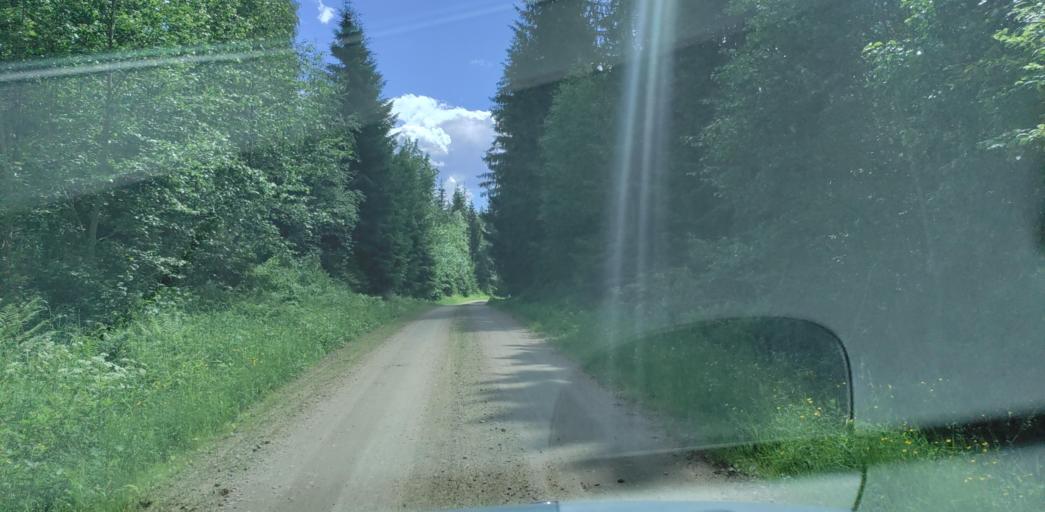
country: SE
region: Vaermland
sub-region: Hagfors Kommun
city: Ekshaerad
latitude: 60.0967
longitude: 13.3169
